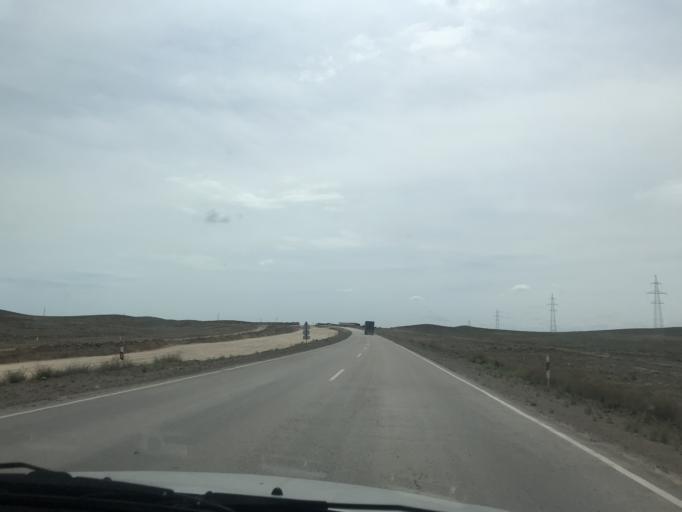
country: KZ
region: Zhambyl
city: Mynaral
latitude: 45.3476
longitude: 73.6916
